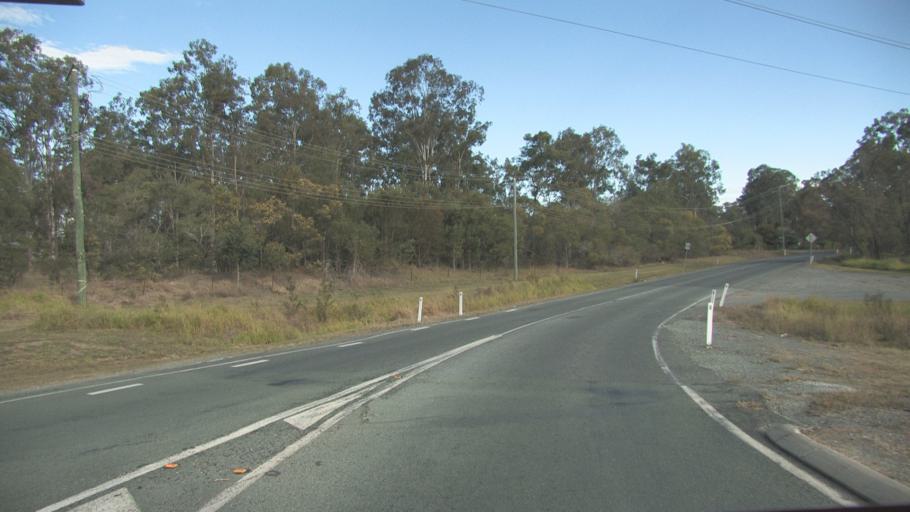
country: AU
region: Queensland
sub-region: Logan
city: North Maclean
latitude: -27.8064
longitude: 153.0610
